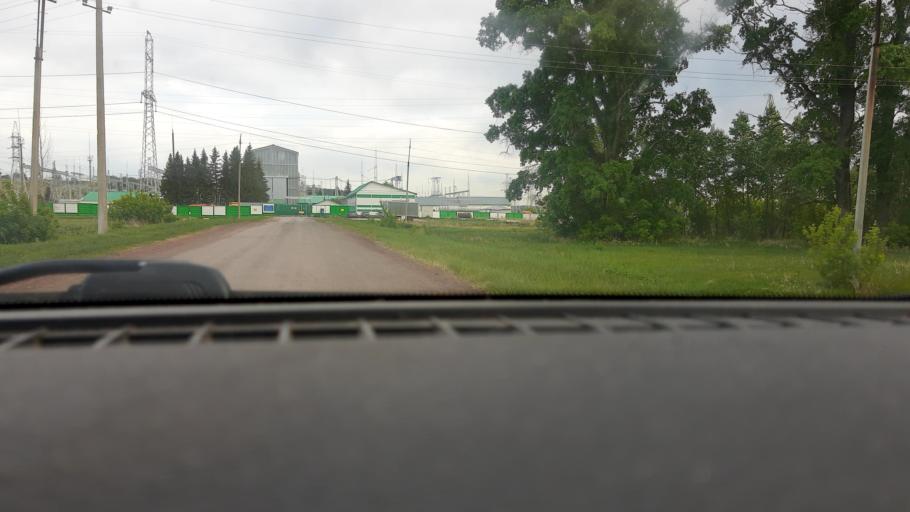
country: RU
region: Bashkortostan
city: Avdon
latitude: 54.4324
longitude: 55.8254
